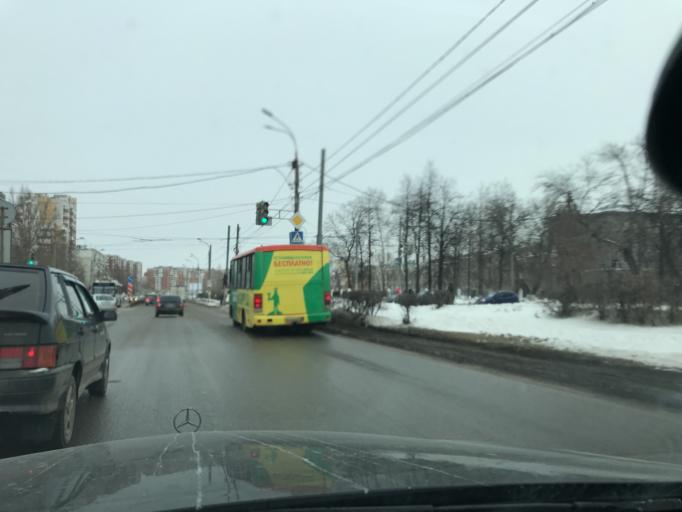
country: RU
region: Nizjnij Novgorod
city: Gorbatovka
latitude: 56.2527
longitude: 43.8523
